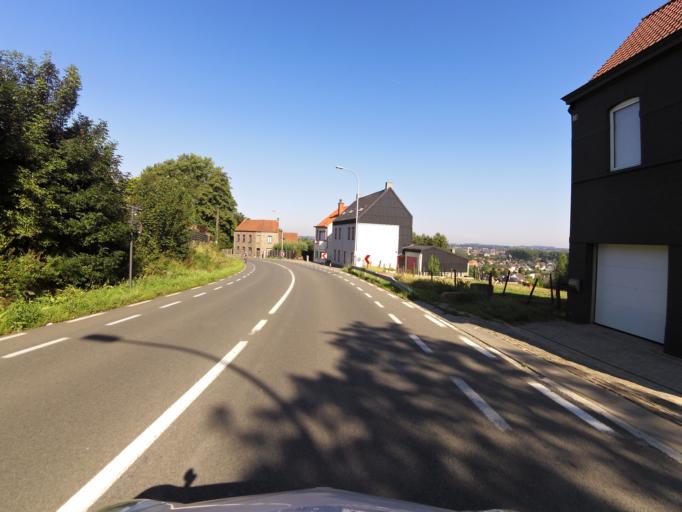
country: BE
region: Flanders
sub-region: Provincie Oost-Vlaanderen
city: Oudenaarde
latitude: 50.8372
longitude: 3.6194
